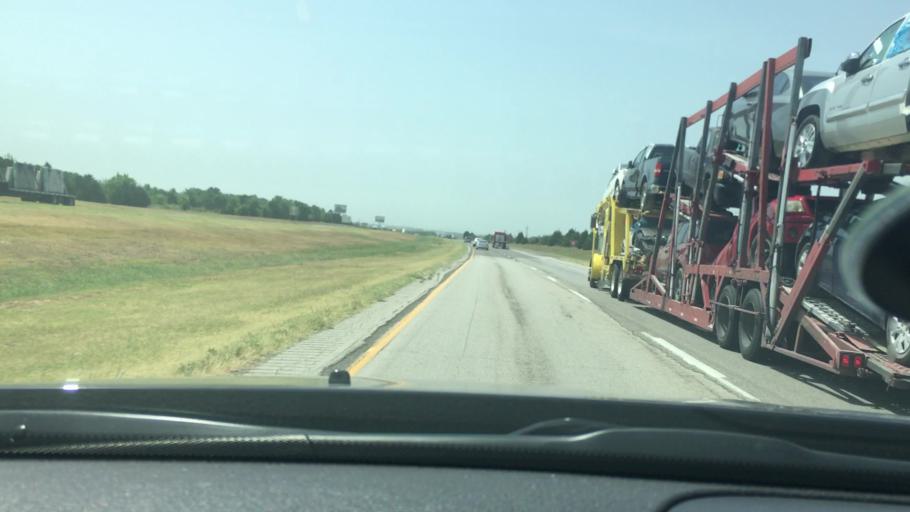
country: US
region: Oklahoma
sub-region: Garvin County
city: Wynnewood
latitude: 34.6207
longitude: -97.2162
